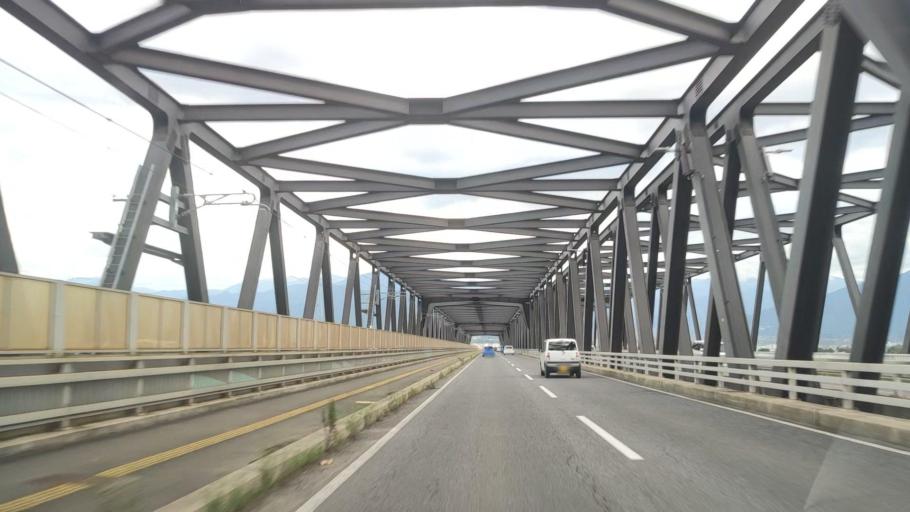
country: JP
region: Nagano
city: Suzaka
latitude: 36.6624
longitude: 138.2711
